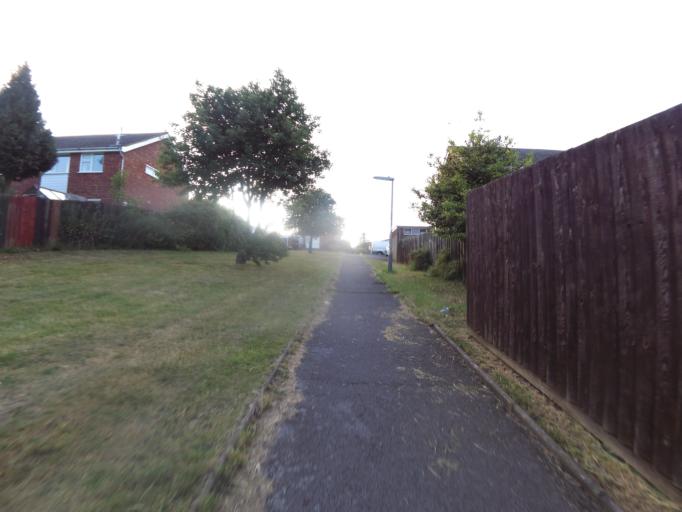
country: GB
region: England
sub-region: Suffolk
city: Ipswich
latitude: 52.0410
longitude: 1.1409
